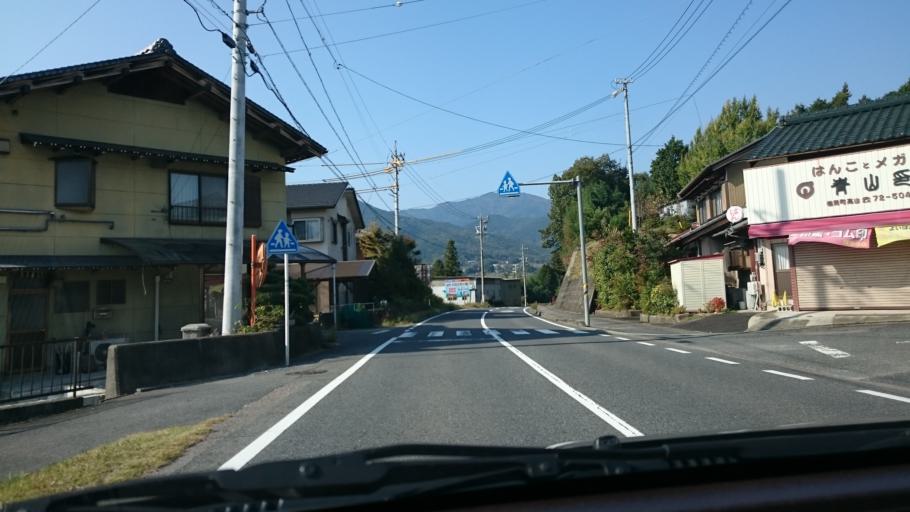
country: JP
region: Gifu
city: Nakatsugawa
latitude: 35.5346
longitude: 137.4508
